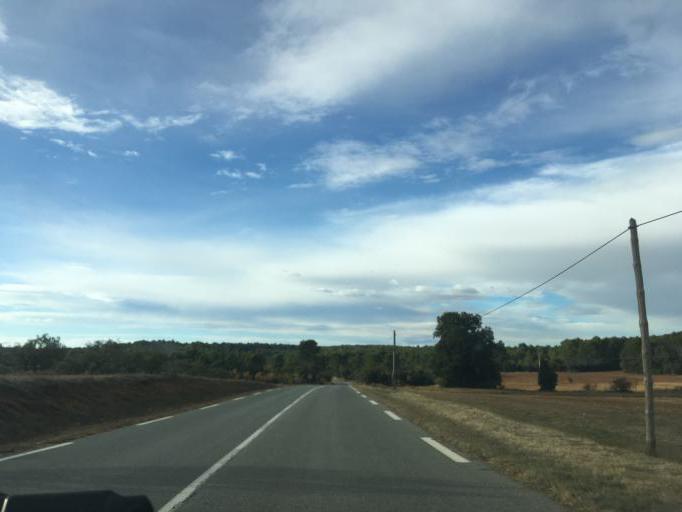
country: FR
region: Provence-Alpes-Cote d'Azur
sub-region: Departement du Var
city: Villecroze
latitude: 43.5987
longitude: 6.2455
